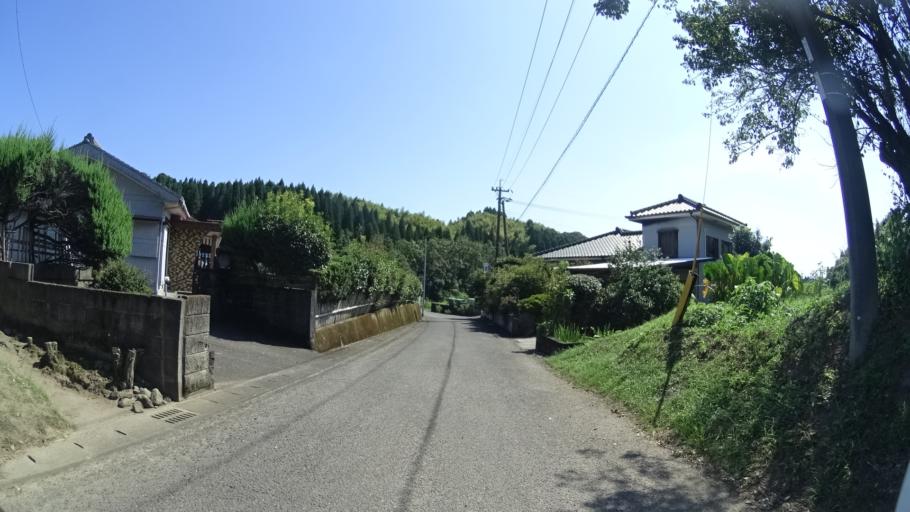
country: JP
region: Kagoshima
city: Kajiki
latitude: 31.7553
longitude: 130.6748
